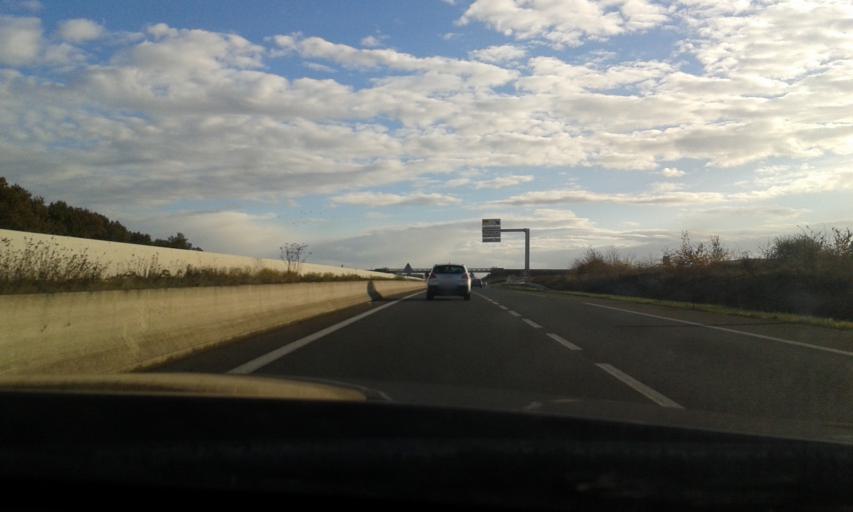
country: FR
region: Centre
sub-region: Departement d'Eure-et-Loir
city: Villemeux-sur-Eure
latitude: 48.6100
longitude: 1.4197
